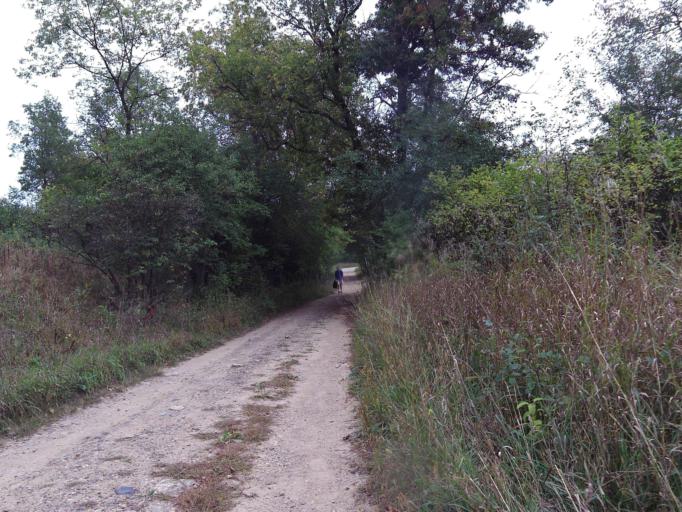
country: US
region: Minnesota
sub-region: Washington County
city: Afton
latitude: 44.8691
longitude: -92.7858
